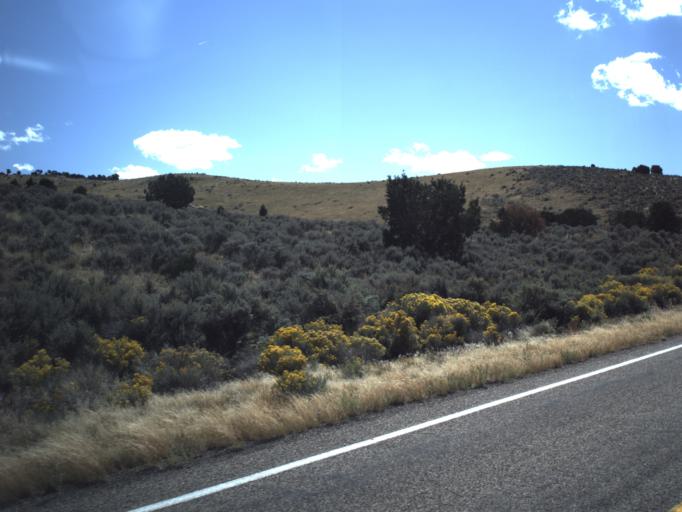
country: US
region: Utah
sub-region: Iron County
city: Parowan
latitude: 38.1052
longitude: -112.9478
